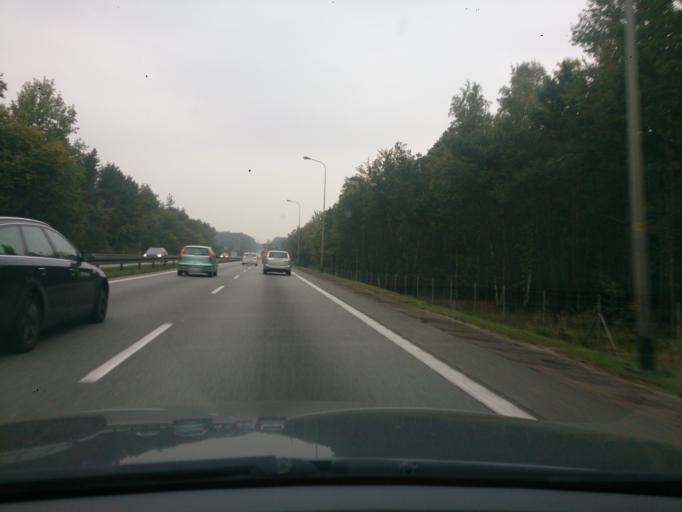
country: PL
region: Pomeranian Voivodeship
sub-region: Sopot
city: Sopot
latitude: 54.3835
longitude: 18.5055
